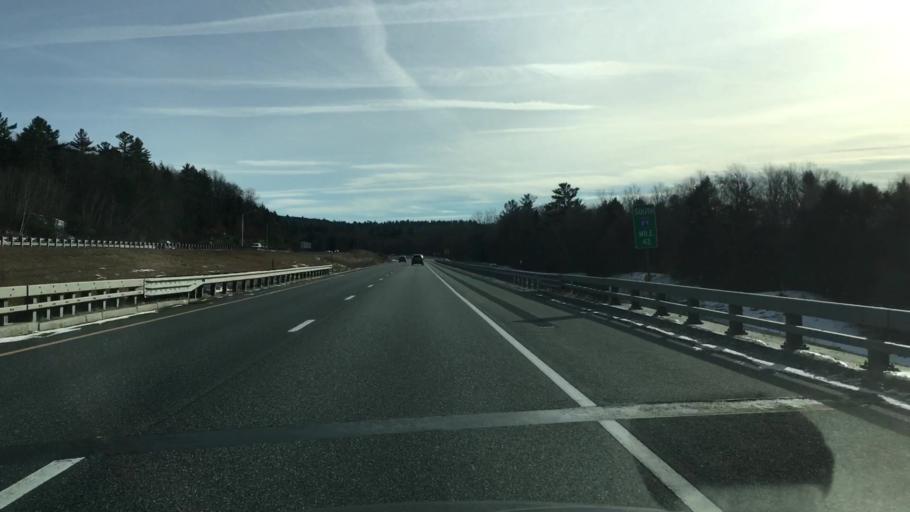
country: US
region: New Hampshire
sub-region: Sullivan County
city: Grantham
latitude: 43.4983
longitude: -72.1330
